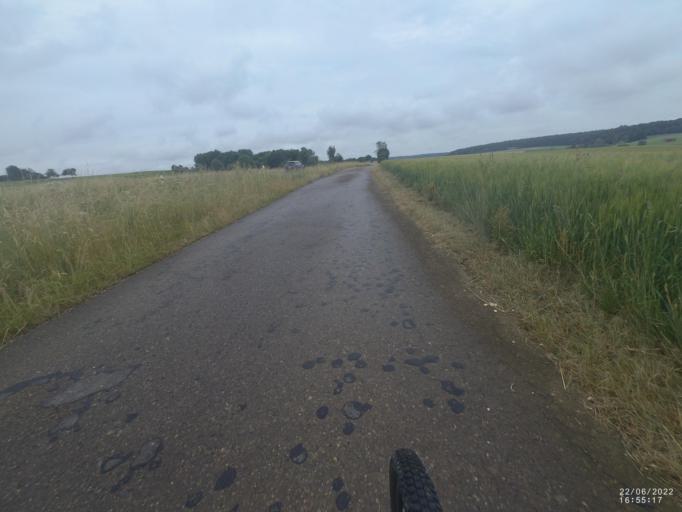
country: DE
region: Baden-Wuerttemberg
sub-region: Regierungsbezirk Stuttgart
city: Gerstetten
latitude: 48.6301
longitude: 10.0239
